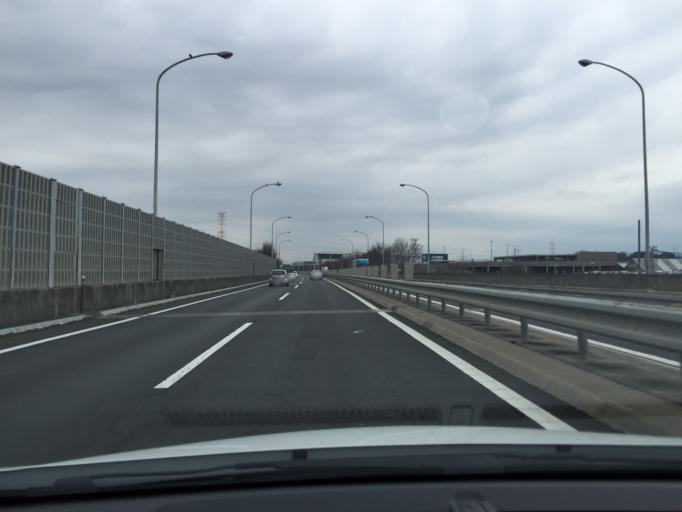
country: JP
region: Saitama
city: Sakado
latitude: 35.9279
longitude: 139.3961
